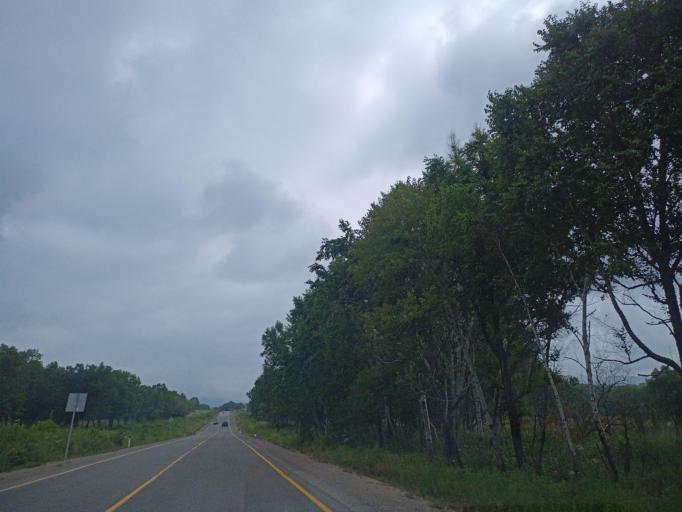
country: RU
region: Primorskiy
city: Dal'nerechensk
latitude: 46.0392
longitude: 133.8902
